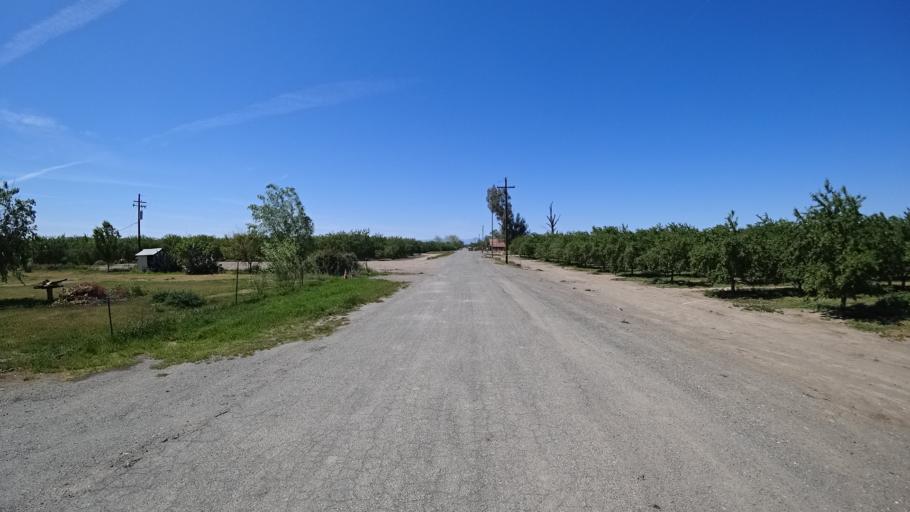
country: US
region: California
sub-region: Glenn County
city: Hamilton City
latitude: 39.7215
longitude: -122.0889
